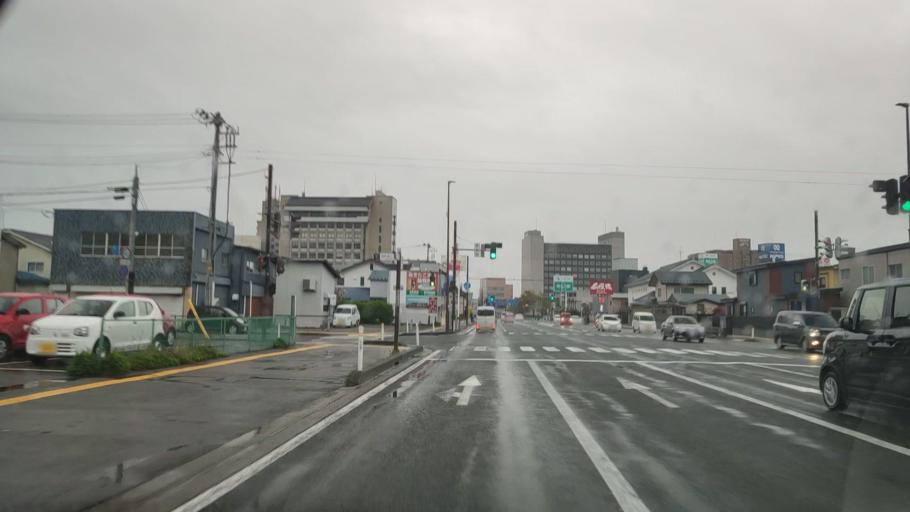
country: JP
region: Akita
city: Akita Shi
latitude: 39.7223
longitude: 140.1089
